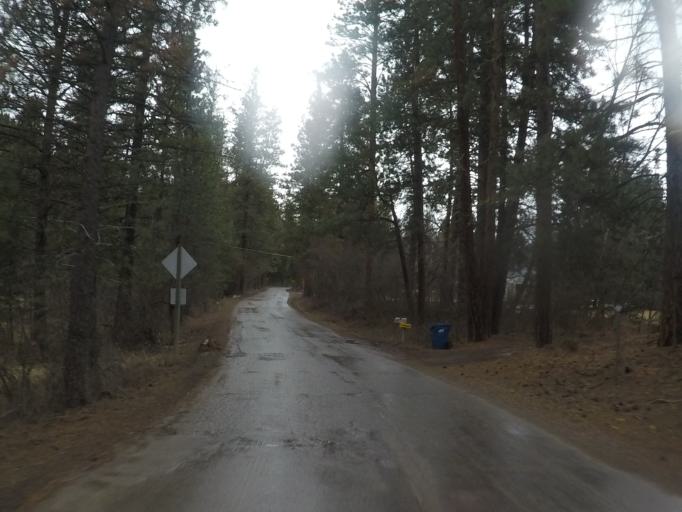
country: US
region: Montana
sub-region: Missoula County
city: East Missoula
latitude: 46.9188
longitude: -113.9597
